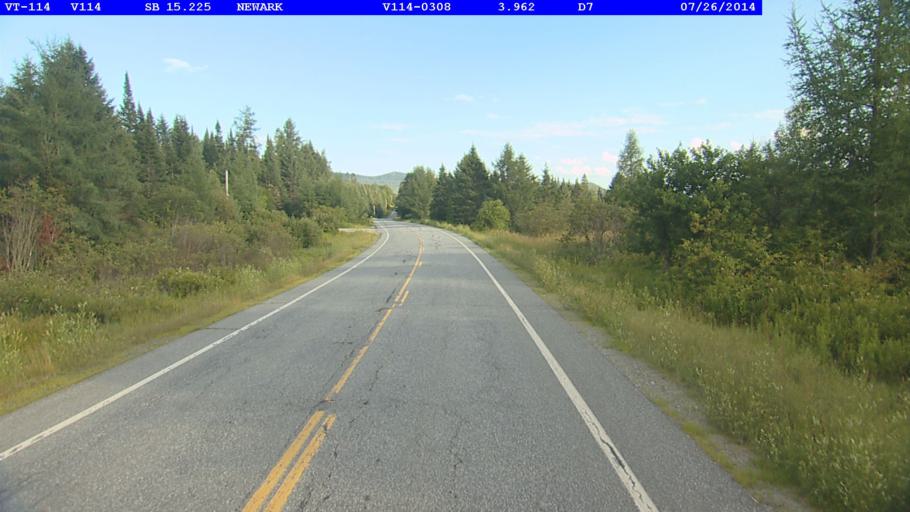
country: US
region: Vermont
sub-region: Caledonia County
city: Lyndonville
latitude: 44.7231
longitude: -71.8733
